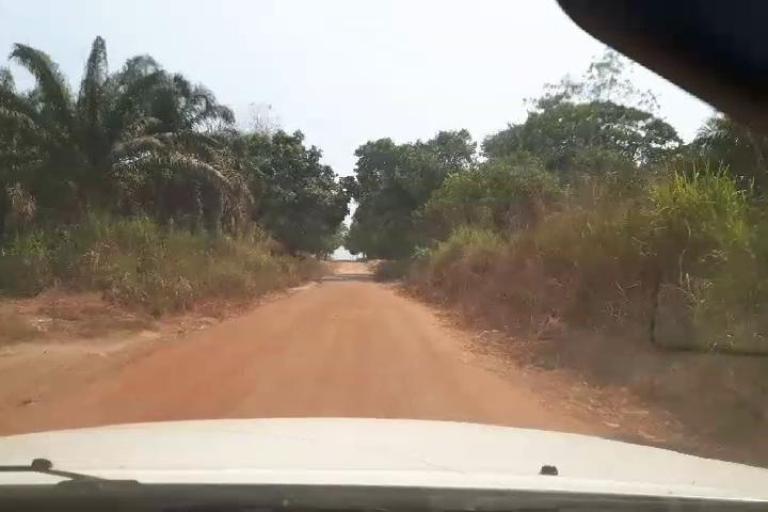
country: SL
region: Northern Province
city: Bumbuna
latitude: 9.0158
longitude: -11.7663
